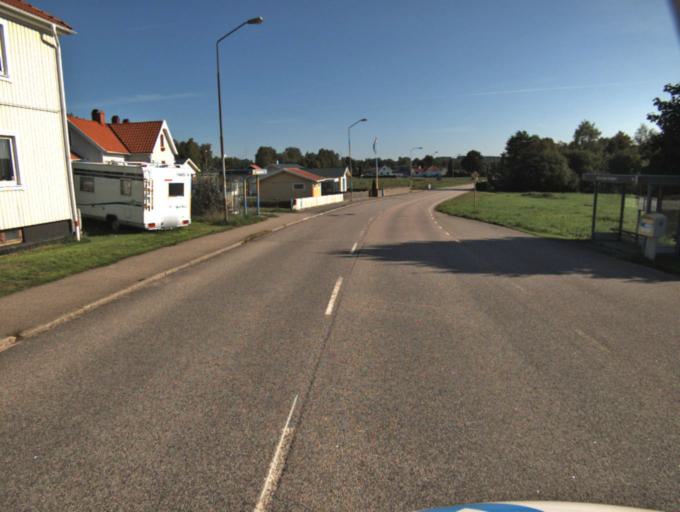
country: SE
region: Vaestra Goetaland
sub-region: Ulricehamns Kommun
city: Ulricehamn
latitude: 57.8033
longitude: 13.4003
